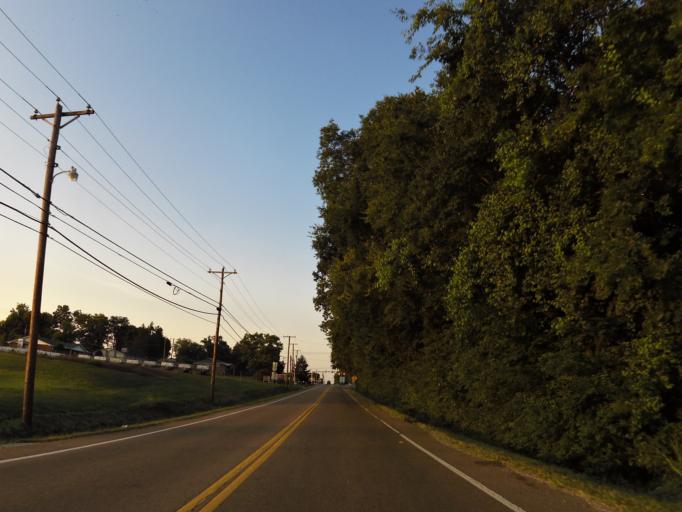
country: US
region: Tennessee
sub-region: Loudon County
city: Loudon
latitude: 35.7161
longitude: -84.3601
